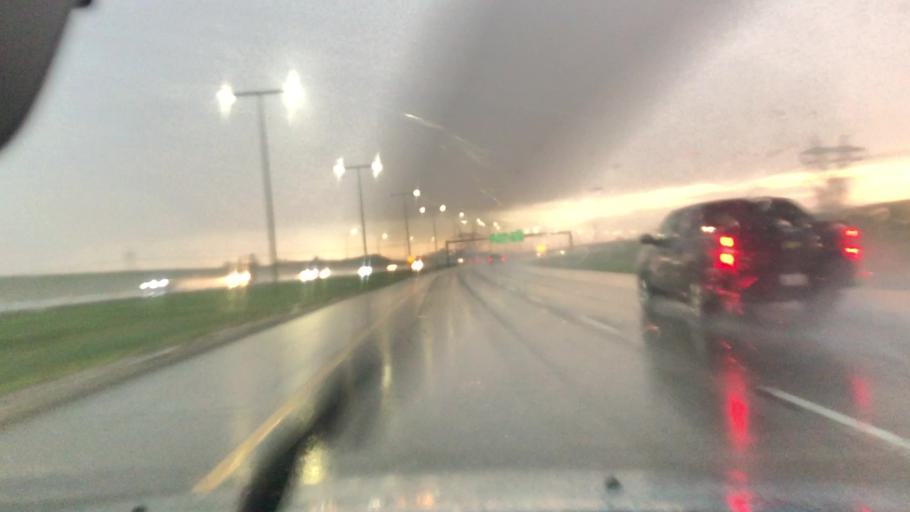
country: CA
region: Alberta
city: Edmonton
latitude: 53.4287
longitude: -113.5655
